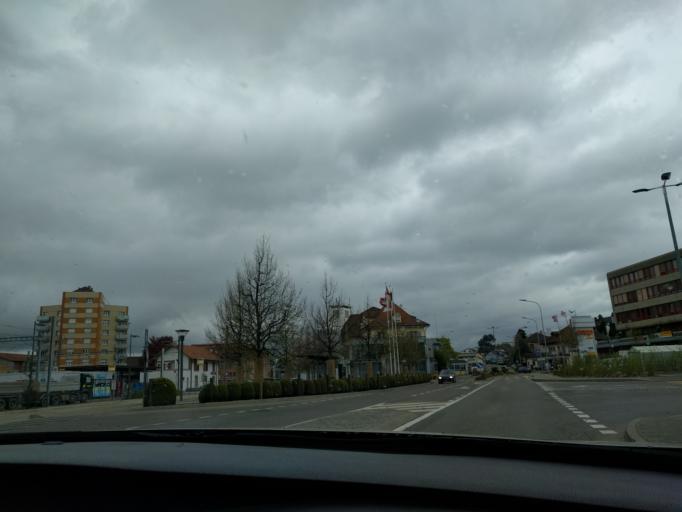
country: CH
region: Fribourg
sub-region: Sense District
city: Dudingen
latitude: 46.8500
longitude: 7.1896
